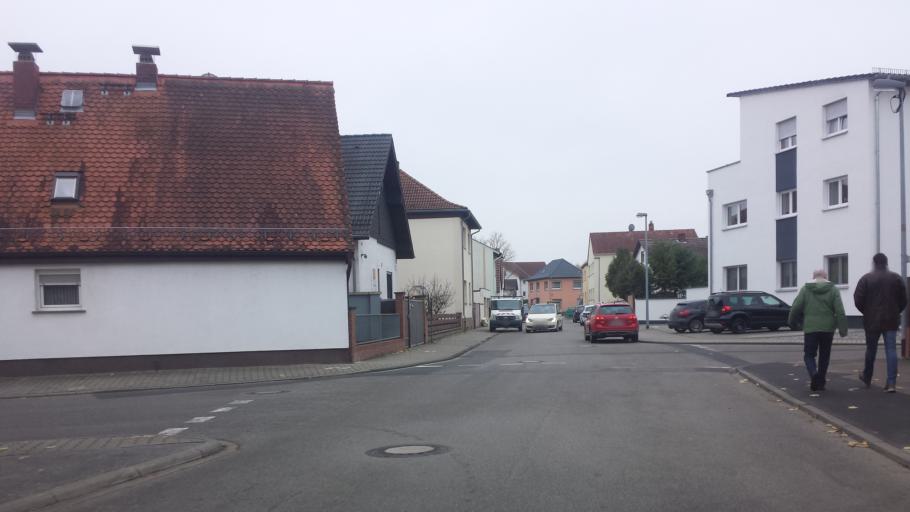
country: DE
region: Hesse
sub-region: Regierungsbezirk Darmstadt
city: Burstadt
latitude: 49.6639
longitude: 8.4442
